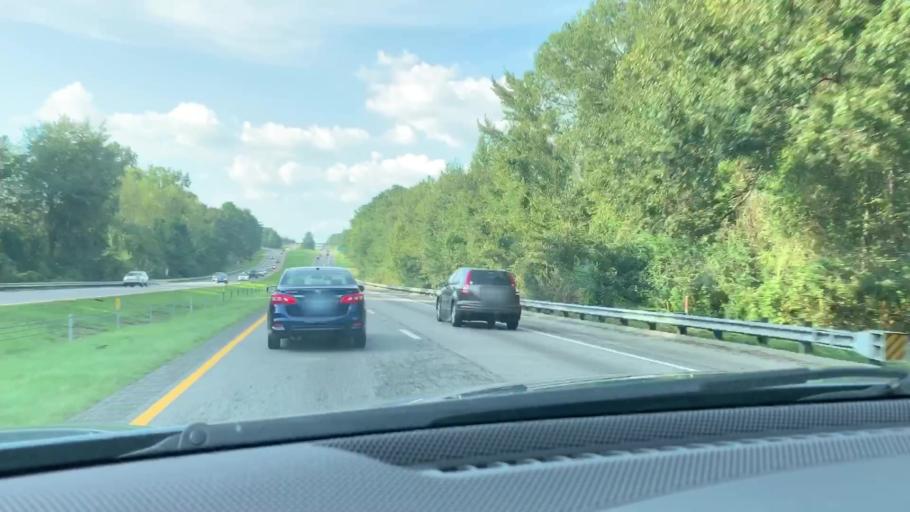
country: US
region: South Carolina
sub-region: Calhoun County
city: Saint Matthews
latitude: 33.6257
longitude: -80.8715
